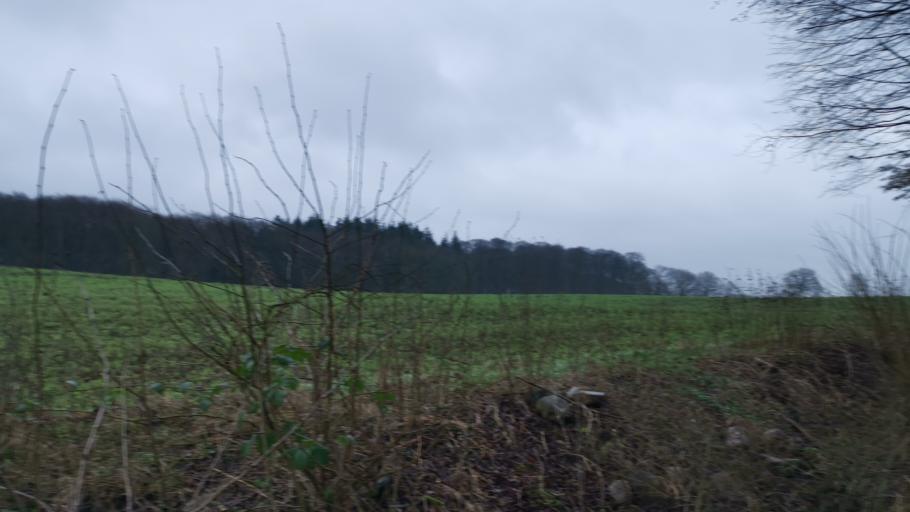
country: DE
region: Schleswig-Holstein
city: Sterley
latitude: 53.6022
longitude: 10.7869
